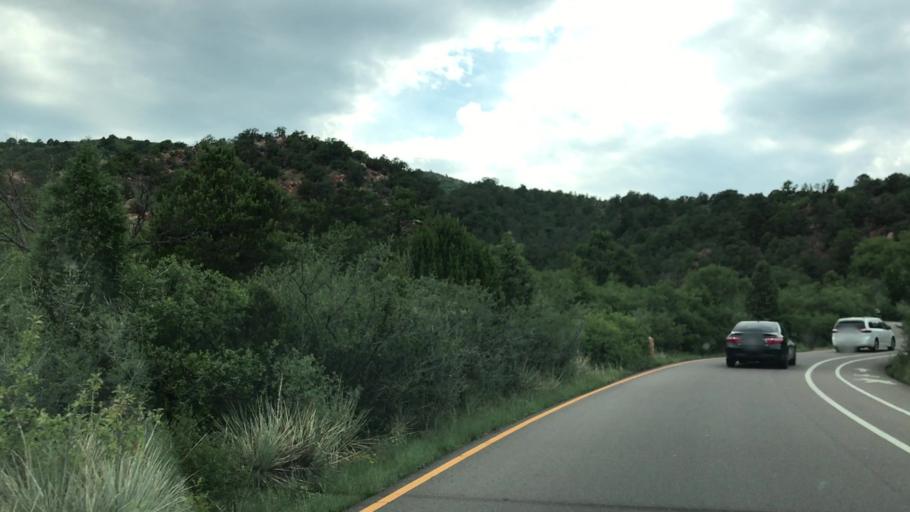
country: US
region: Colorado
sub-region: El Paso County
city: Manitou Springs
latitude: 38.8819
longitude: -104.8819
